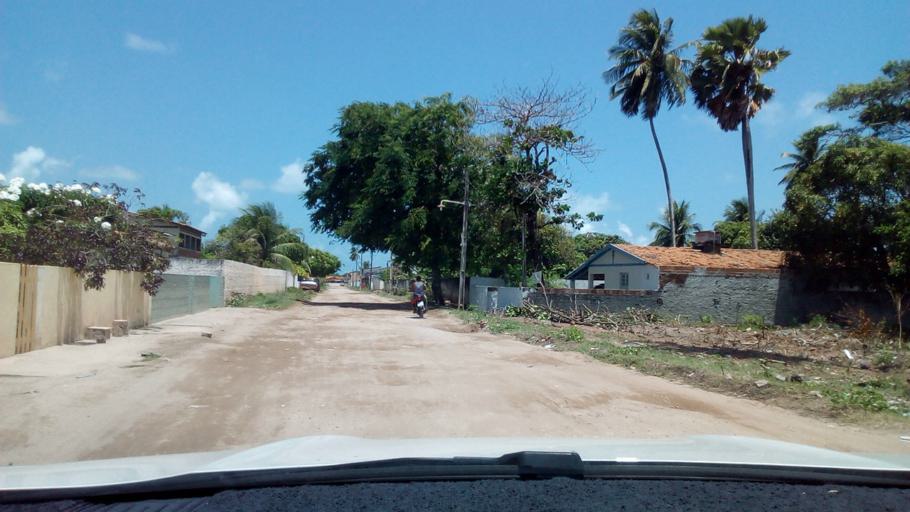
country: BR
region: Paraiba
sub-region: Pitimbu
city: Pitimbu
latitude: -7.5235
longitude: -34.8184
